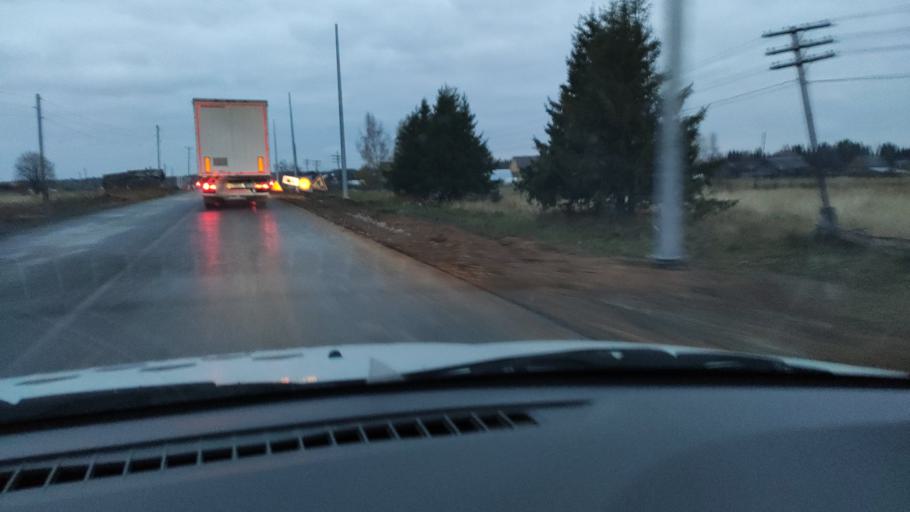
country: RU
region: Kirov
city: Kostino
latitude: 58.8330
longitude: 53.3064
